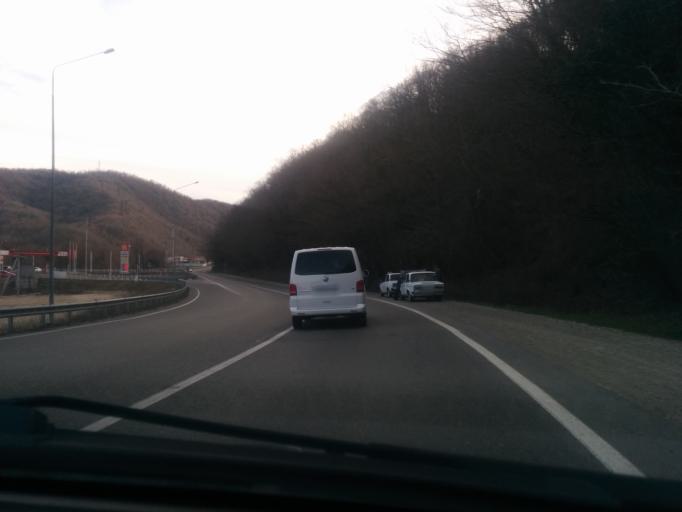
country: RU
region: Krasnodarskiy
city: Ol'ginka
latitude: 44.2186
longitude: 38.8939
